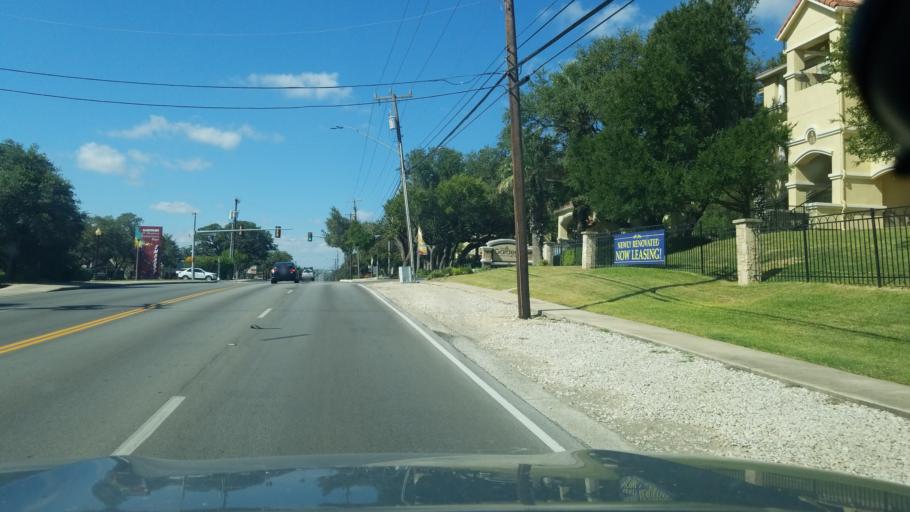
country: US
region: Texas
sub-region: Bexar County
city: Hollywood Park
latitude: 29.5663
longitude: -98.4887
